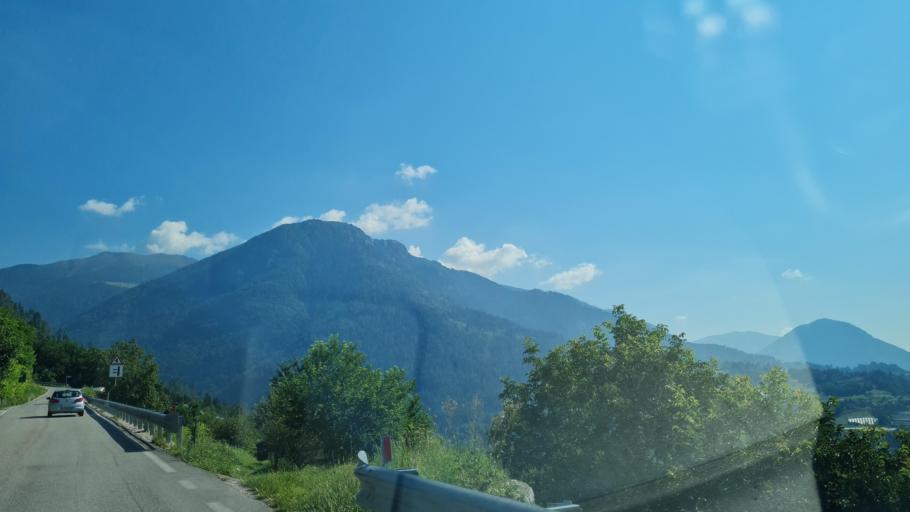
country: IT
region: Trentino-Alto Adige
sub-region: Provincia di Trento
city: Telve
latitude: 46.0775
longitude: 11.4851
